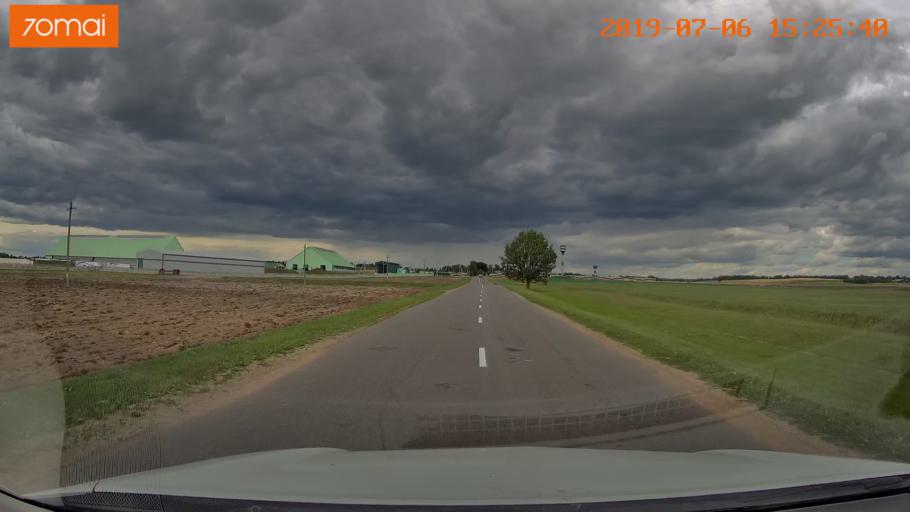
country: BY
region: Minsk
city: Valozhyn
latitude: 54.0347
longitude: 26.6047
